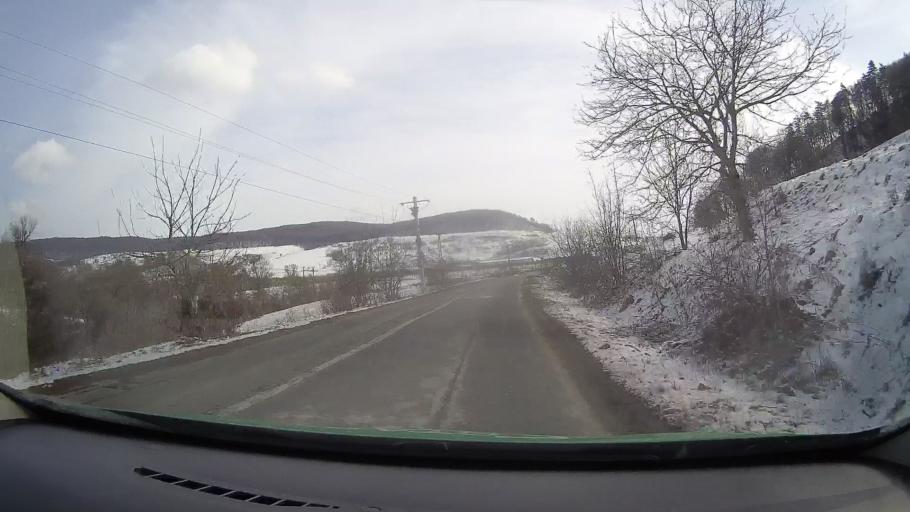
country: RO
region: Mures
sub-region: Comuna Apold
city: Apold
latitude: 46.1404
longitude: 24.8184
